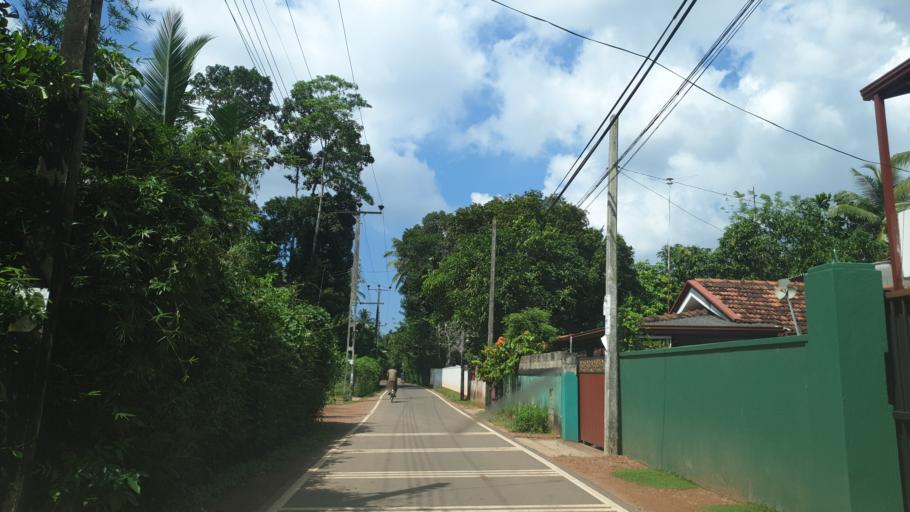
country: LK
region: Western
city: Panadura
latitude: 6.6753
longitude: 79.9729
